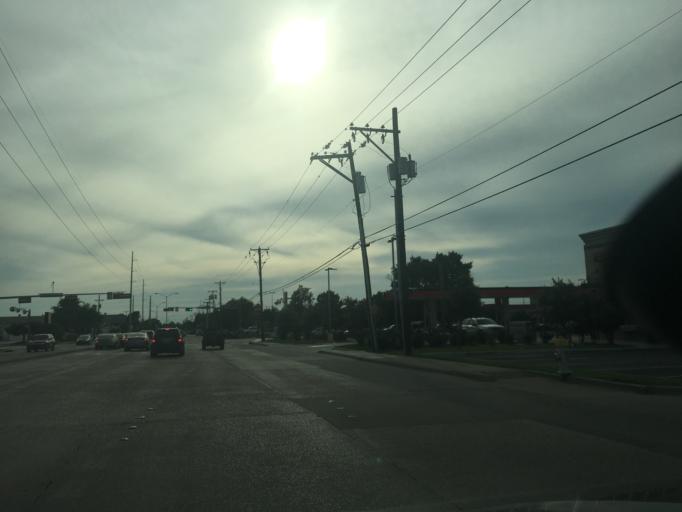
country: US
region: Texas
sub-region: Dallas County
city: Richardson
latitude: 32.9454
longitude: -96.6988
